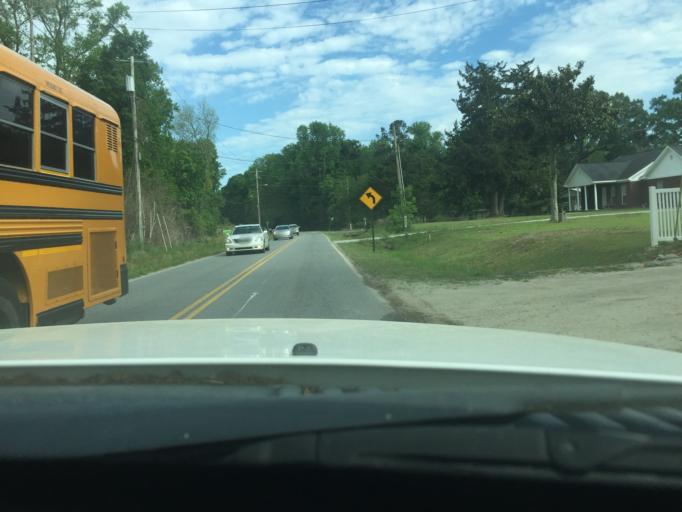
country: US
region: Georgia
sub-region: Chatham County
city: Georgetown
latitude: 31.9812
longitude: -81.2563
